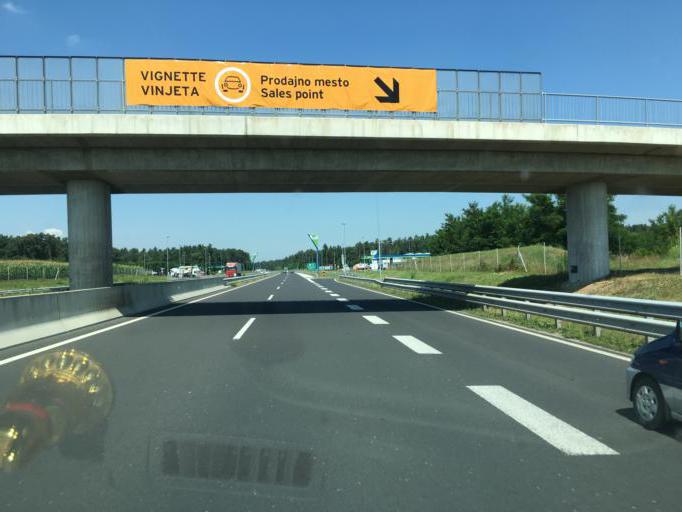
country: SI
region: Kidricevo
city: Kidricevo
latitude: 46.4259
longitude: 15.7975
